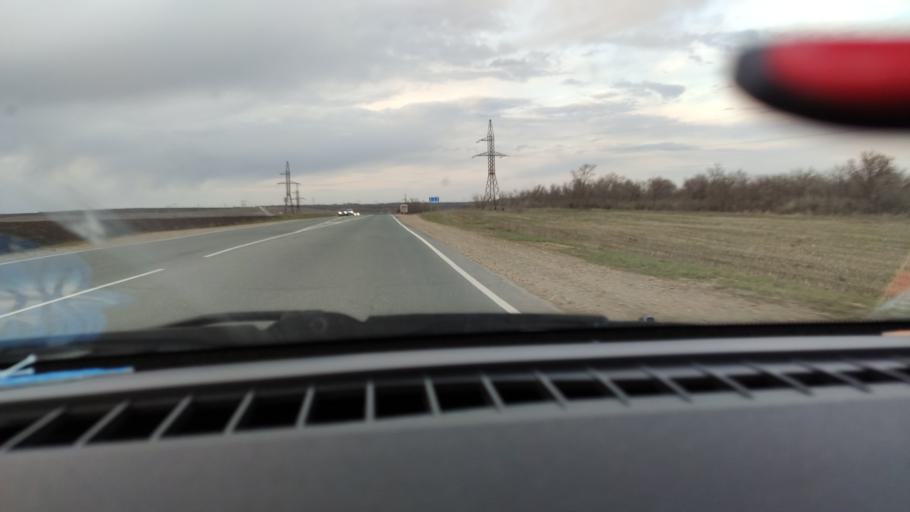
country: RU
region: Saratov
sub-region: Saratovskiy Rayon
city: Saratov
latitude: 51.7491
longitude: 46.0579
